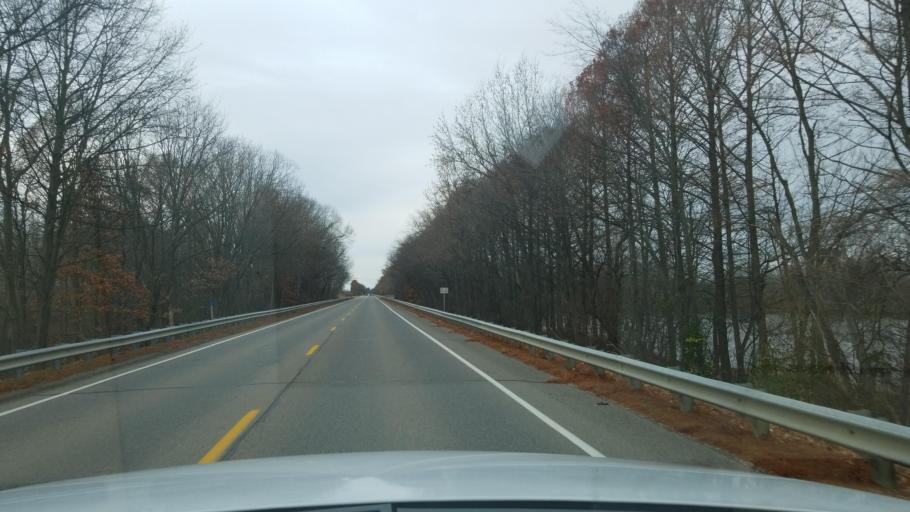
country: US
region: Indiana
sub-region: Posey County
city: Mount Vernon
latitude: 37.9290
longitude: -87.9780
